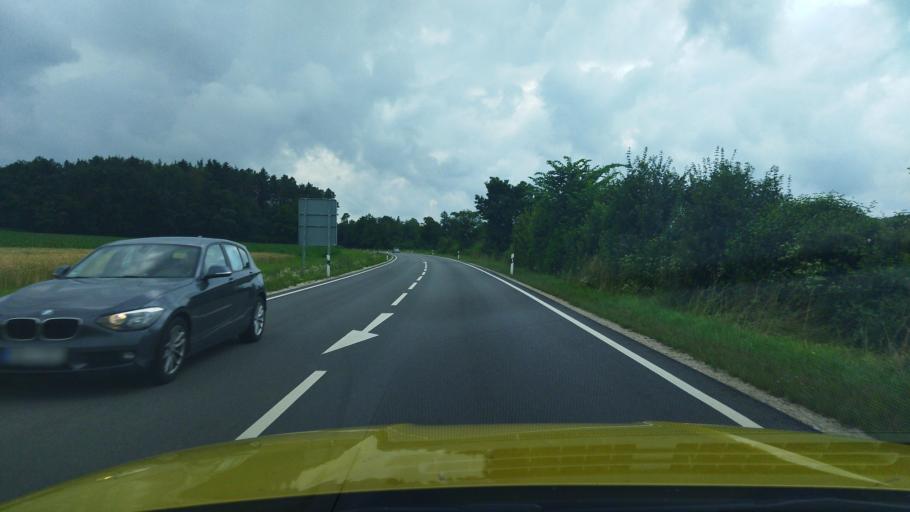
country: DE
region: Bavaria
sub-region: Regierungsbezirk Mittelfranken
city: Absberg
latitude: 49.1101
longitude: 10.9099
